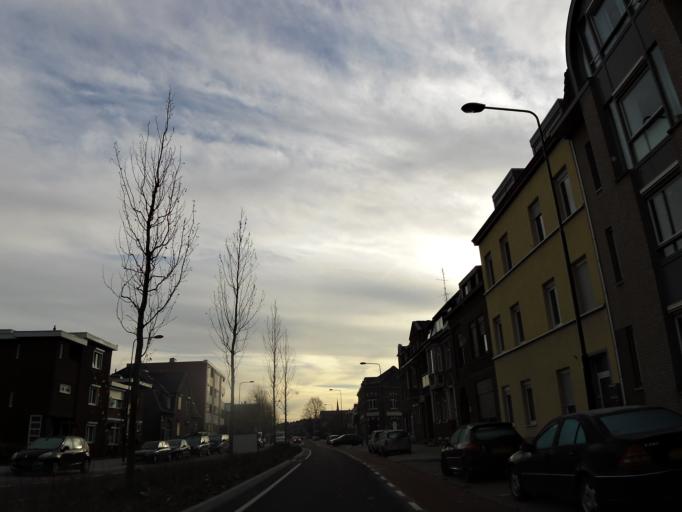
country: NL
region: Limburg
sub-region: Gemeente Vaals
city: Vaals
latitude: 50.7750
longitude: 6.0117
